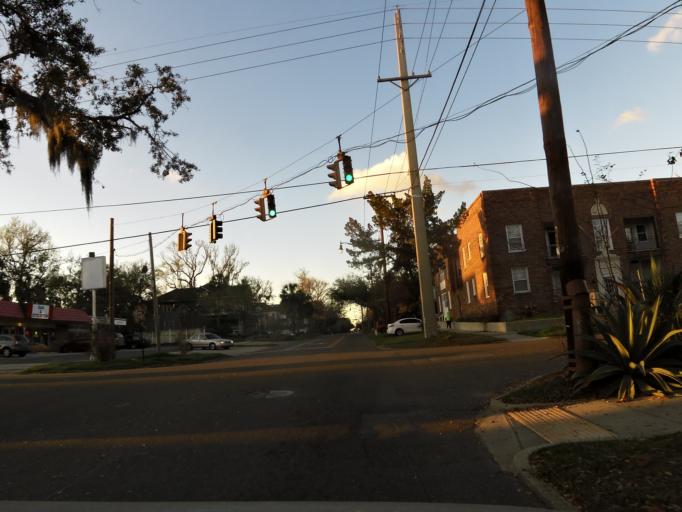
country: US
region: Florida
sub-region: Duval County
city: Jacksonville
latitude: 30.3103
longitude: -81.6879
